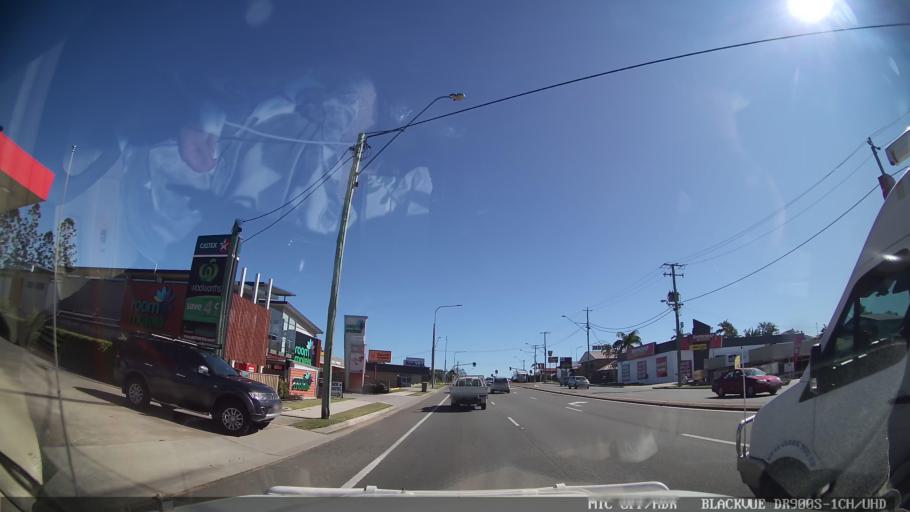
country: AU
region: Queensland
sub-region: Gympie Regional Council
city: Gympie
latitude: -26.1918
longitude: 152.6574
